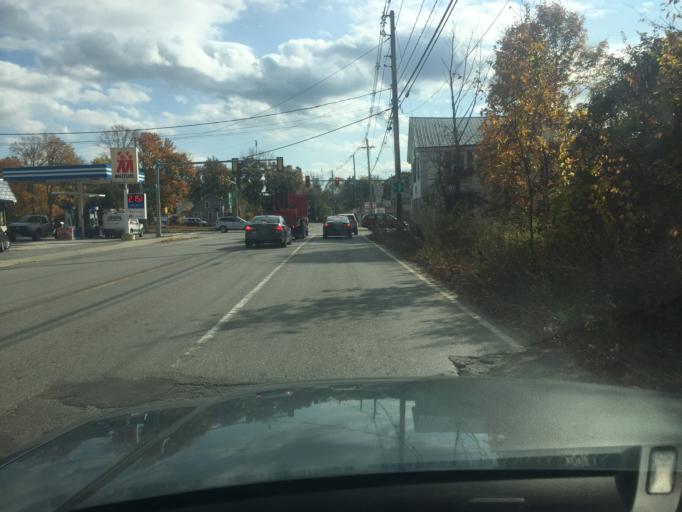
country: US
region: Massachusetts
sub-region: Norfolk County
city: Bellingham
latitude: 42.1035
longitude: -71.5043
